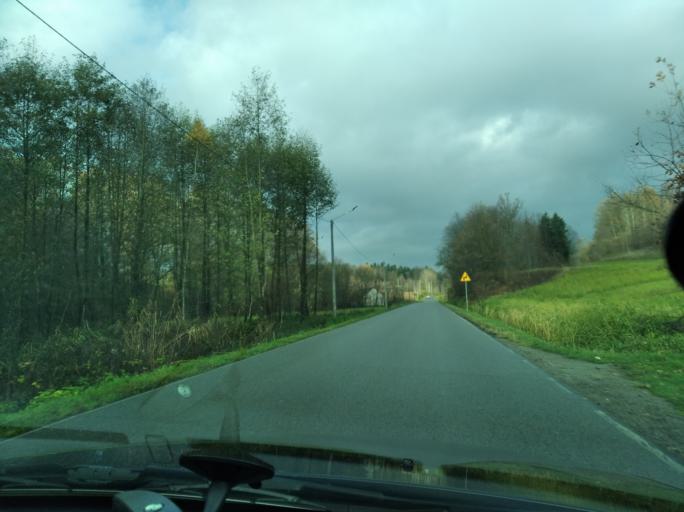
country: PL
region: Subcarpathian Voivodeship
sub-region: Powiat strzyzowski
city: Wisniowa
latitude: 49.9230
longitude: 21.7177
